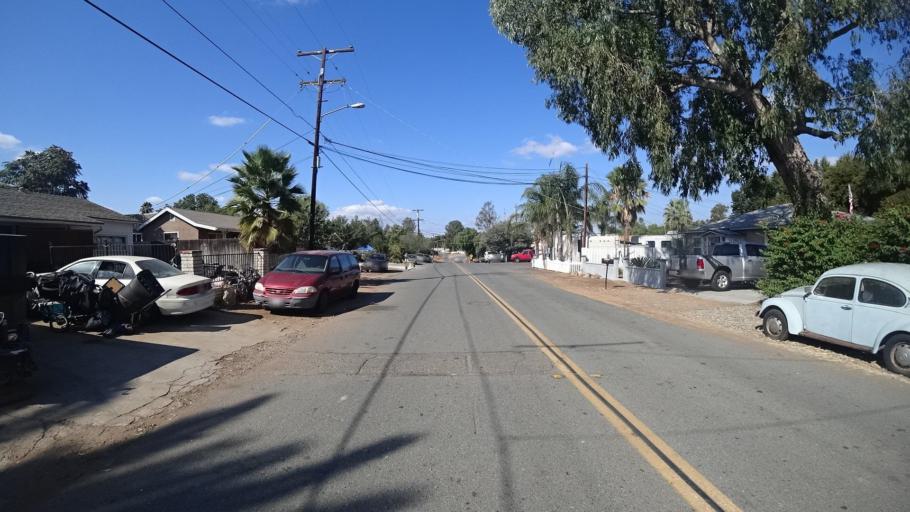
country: US
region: California
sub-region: San Diego County
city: Lakeside
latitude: 32.8566
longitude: -116.9171
